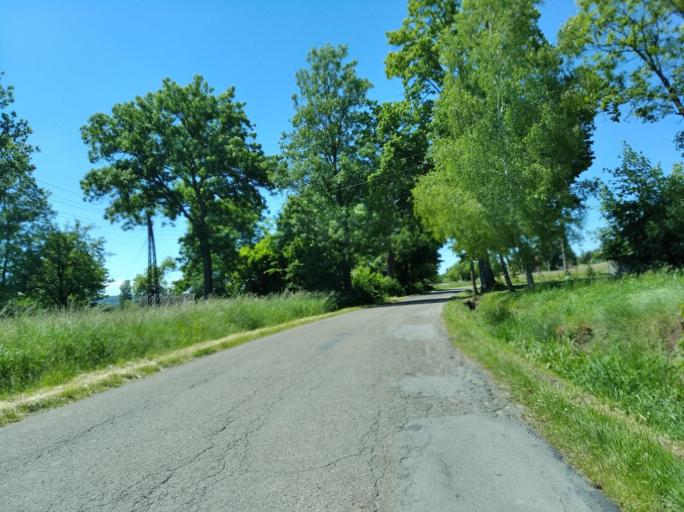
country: PL
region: Subcarpathian Voivodeship
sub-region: Powiat jasielski
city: Nowy Zmigrod
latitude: 49.6311
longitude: 21.5897
